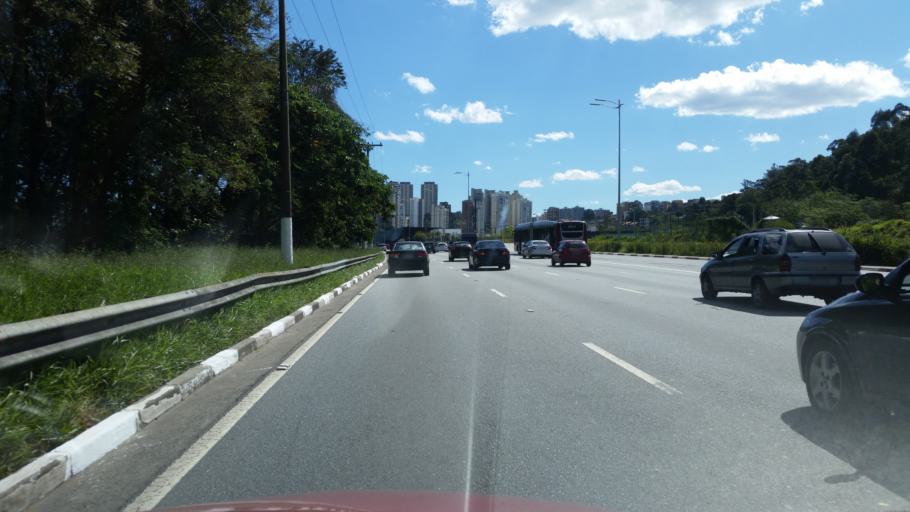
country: BR
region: Sao Paulo
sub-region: Taboao Da Serra
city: Taboao da Serra
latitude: -23.6231
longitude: -46.7080
